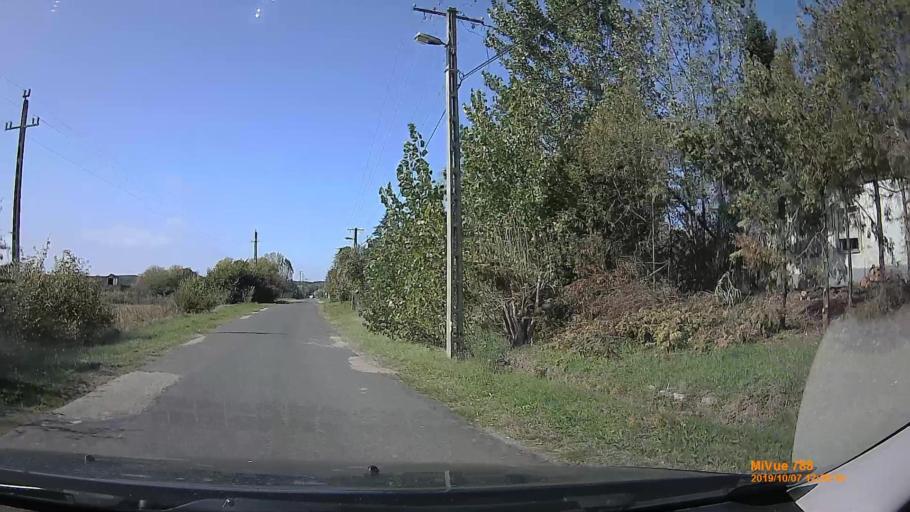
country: HU
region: Bacs-Kiskun
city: Tiszakecske
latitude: 46.8829
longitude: 20.1296
